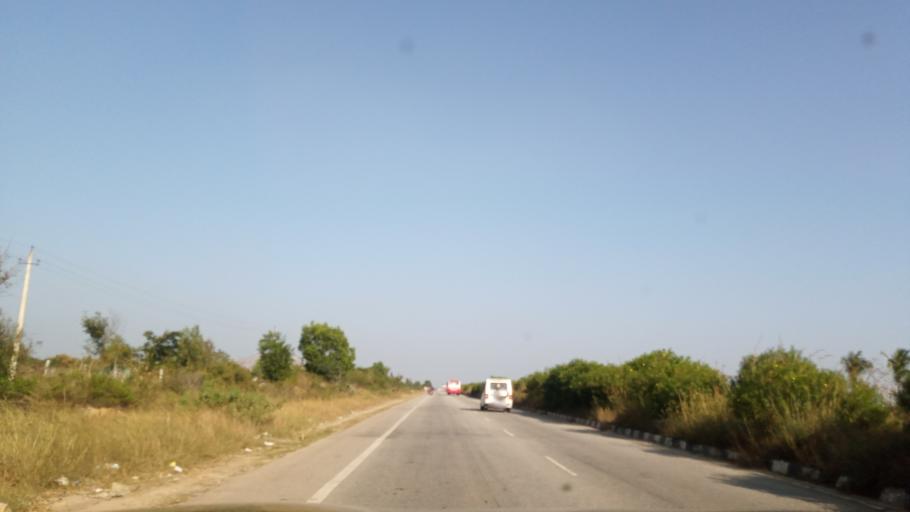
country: IN
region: Karnataka
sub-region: Kolar
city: Mulbagal
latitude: 13.1547
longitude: 78.3351
